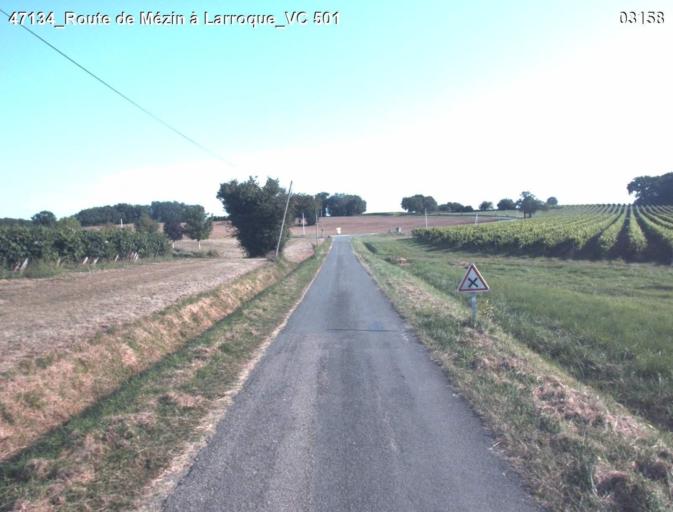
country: FR
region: Aquitaine
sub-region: Departement du Lot-et-Garonne
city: Mezin
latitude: 44.0233
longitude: 0.2706
